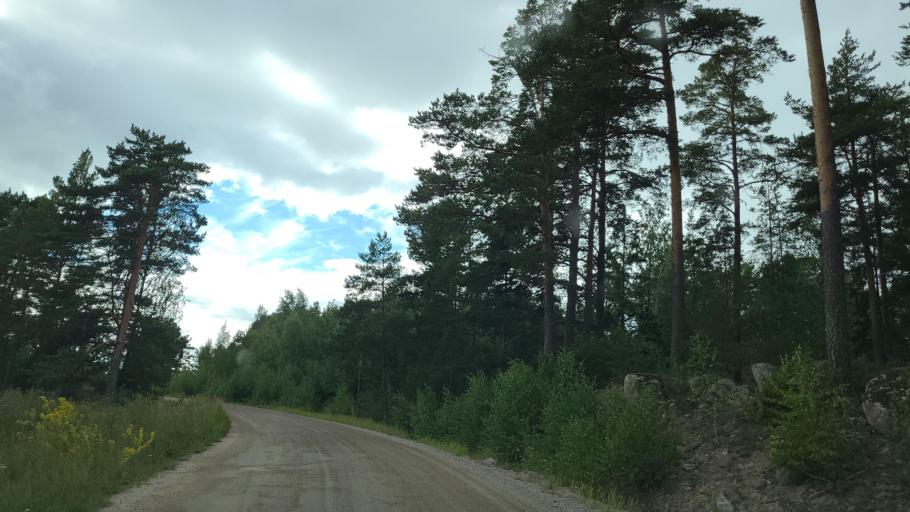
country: FI
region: Varsinais-Suomi
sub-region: Aboland-Turunmaa
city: Nagu
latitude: 60.2058
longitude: 21.8201
